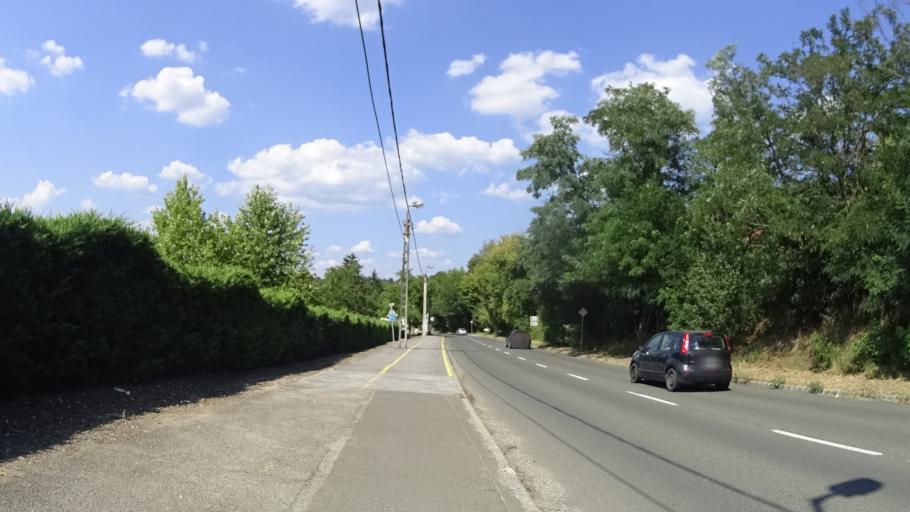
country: HU
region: Komarom-Esztergom
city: Pilismarot
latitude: 47.7923
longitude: 18.9104
